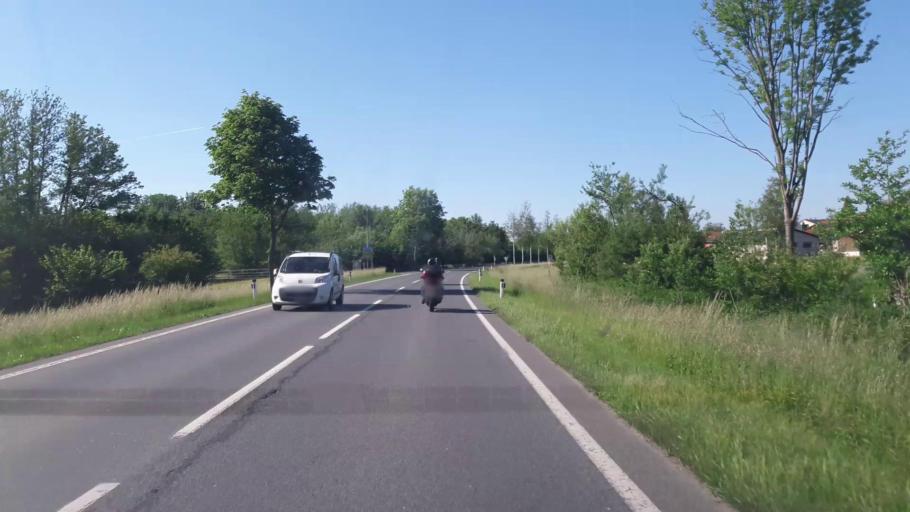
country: AT
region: Burgenland
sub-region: Politischer Bezirk Oberwart
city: Litzelsdorf
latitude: 47.2042
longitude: 16.1601
